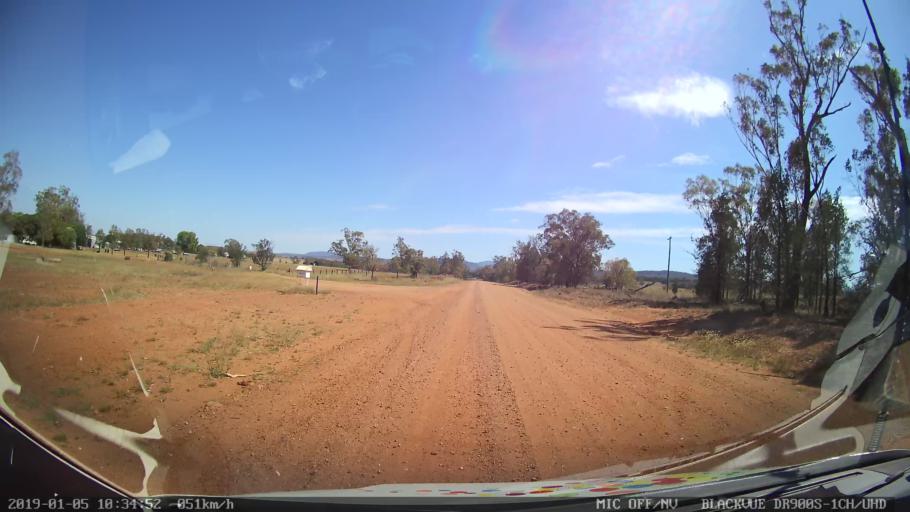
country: AU
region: New South Wales
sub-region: Gilgandra
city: Gilgandra
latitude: -31.4948
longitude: 148.9293
